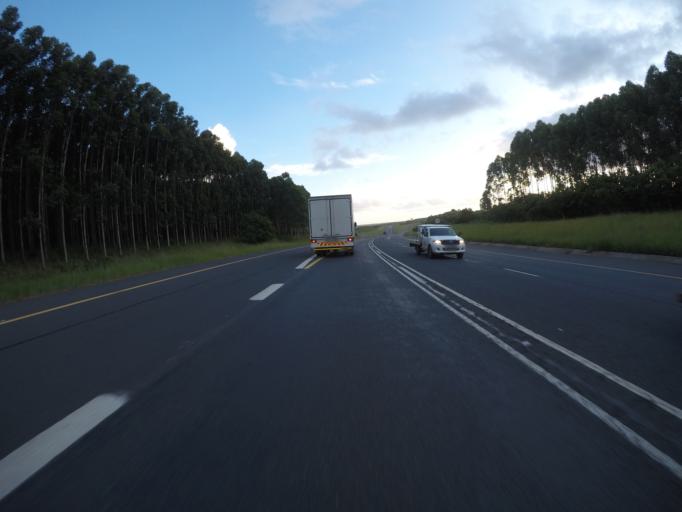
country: ZA
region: KwaZulu-Natal
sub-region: uThungulu District Municipality
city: KwaMbonambi
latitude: -28.5933
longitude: 32.0998
